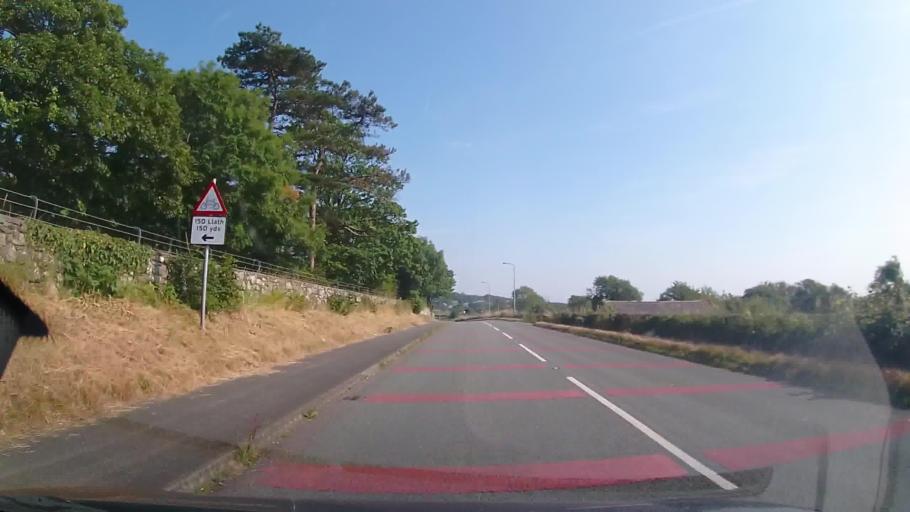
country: GB
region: Wales
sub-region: Gwynedd
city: Llanfair
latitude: 52.8318
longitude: -4.1114
